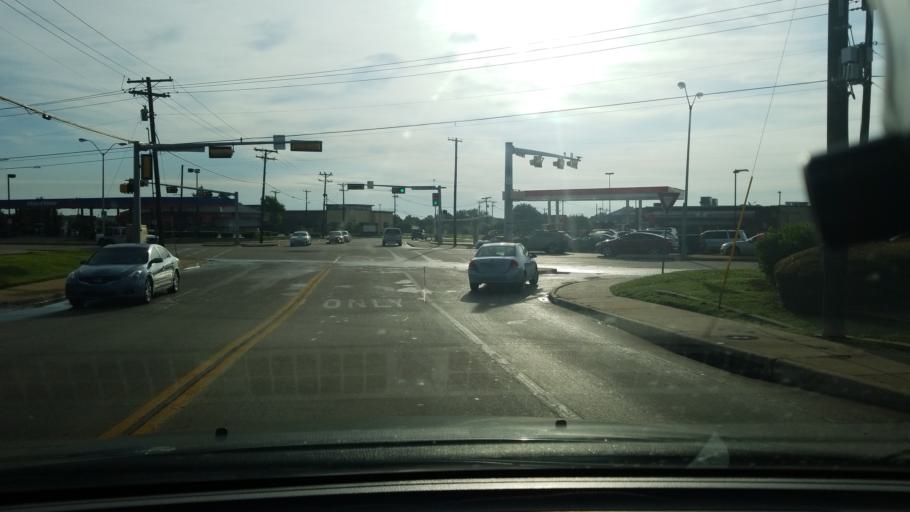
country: US
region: Texas
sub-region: Dallas County
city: Mesquite
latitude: 32.7970
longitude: -96.6123
